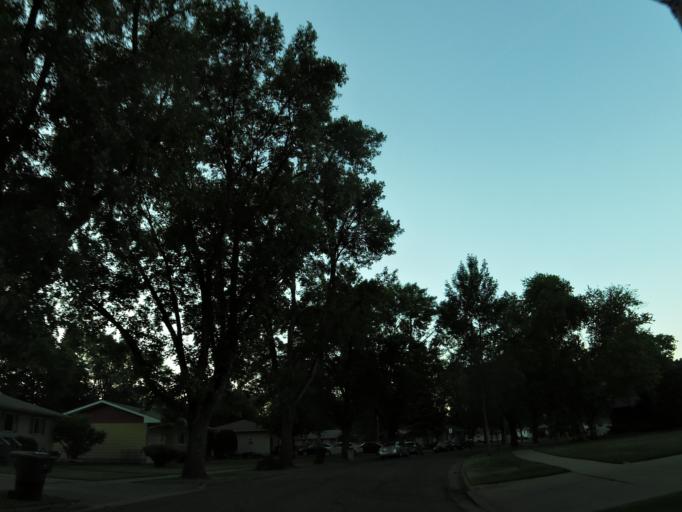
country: US
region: North Dakota
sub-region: Grand Forks County
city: Grand Forks
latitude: 47.9277
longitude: -97.0798
